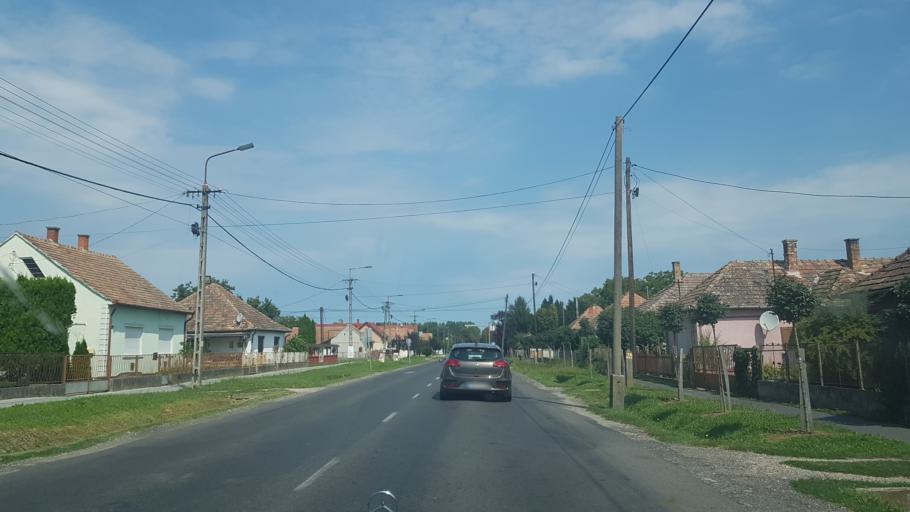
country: HU
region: Somogy
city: Kethely
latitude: 46.6519
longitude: 17.3921
